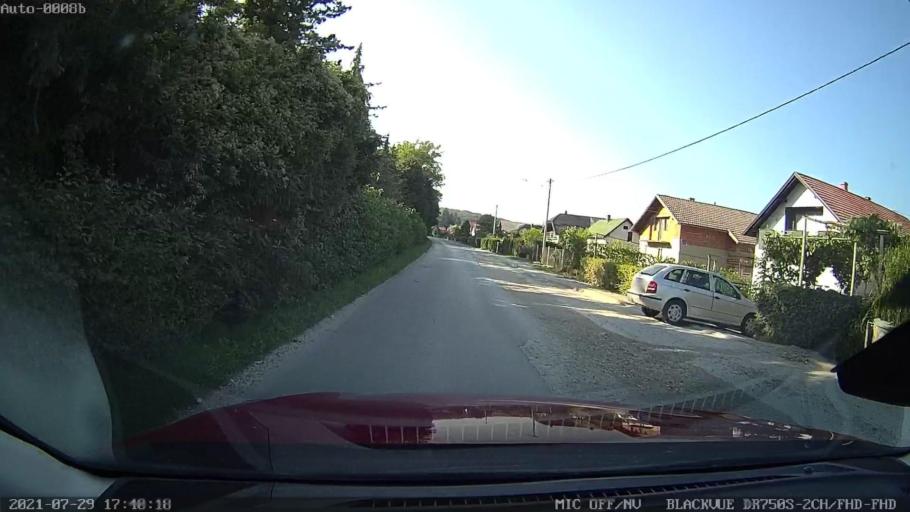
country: HR
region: Varazdinska
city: Vinica
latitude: 46.3212
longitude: 16.1553
